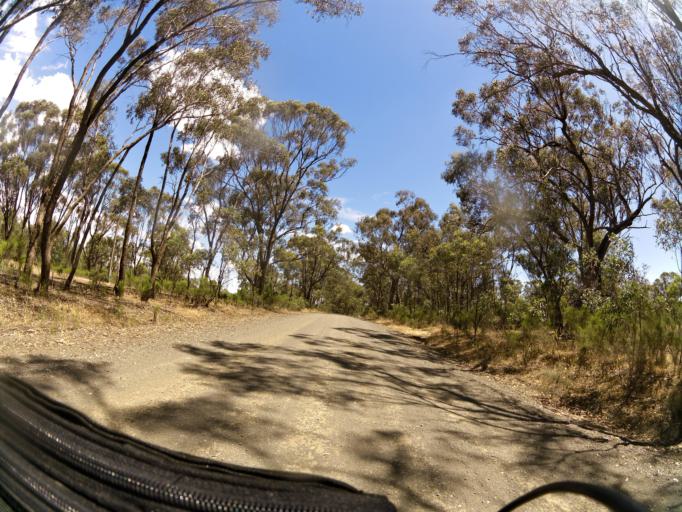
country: AU
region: Victoria
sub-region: Campaspe
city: Kyabram
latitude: -36.8025
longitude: 145.0760
